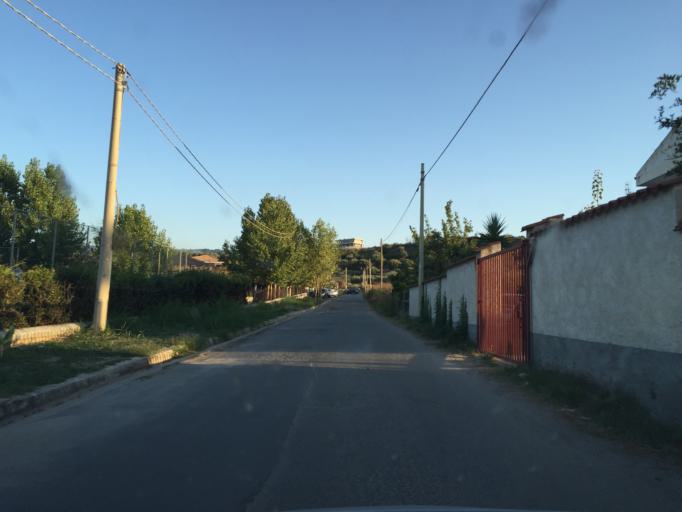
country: IT
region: Calabria
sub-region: Provincia di Vibo-Valentia
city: Briatico
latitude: 38.7202
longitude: 16.0548
